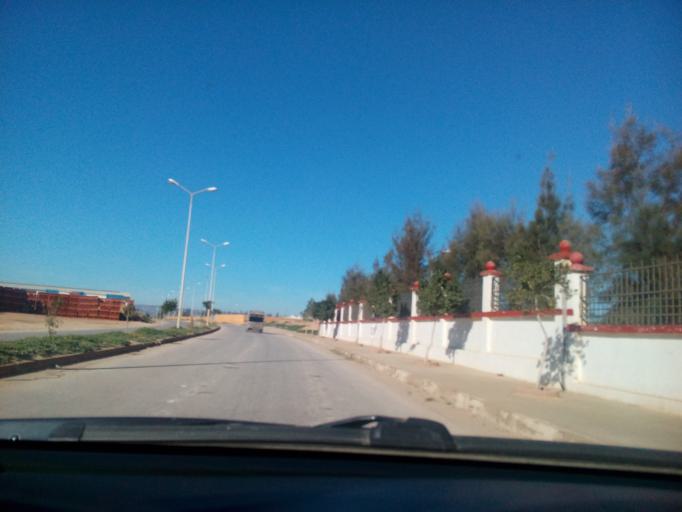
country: DZ
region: Relizane
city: Relizane
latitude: 35.7201
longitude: 0.5288
